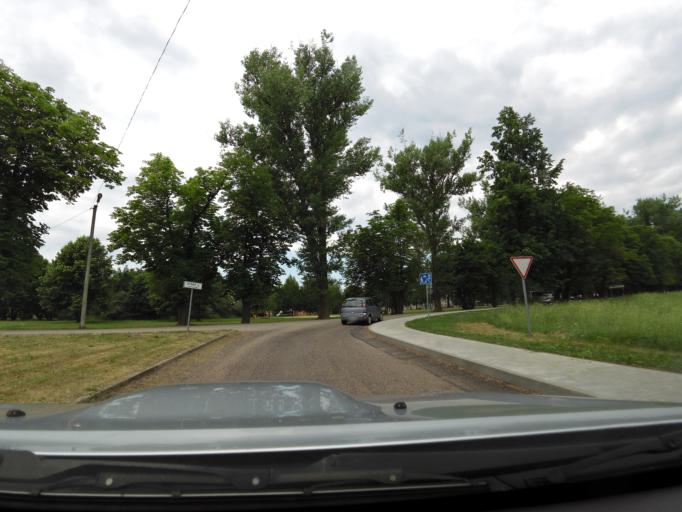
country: LT
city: Vilkaviskis
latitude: 54.6364
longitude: 22.9771
